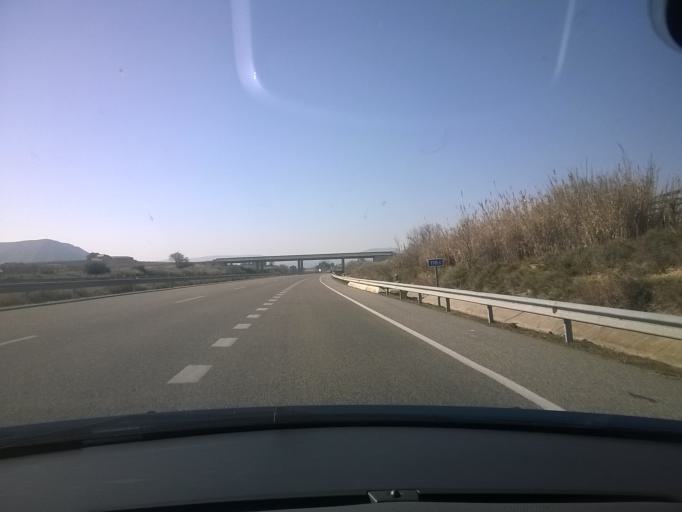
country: ES
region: Catalonia
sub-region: Provincia de Lleida
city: Seros
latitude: 41.4960
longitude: 0.3901
